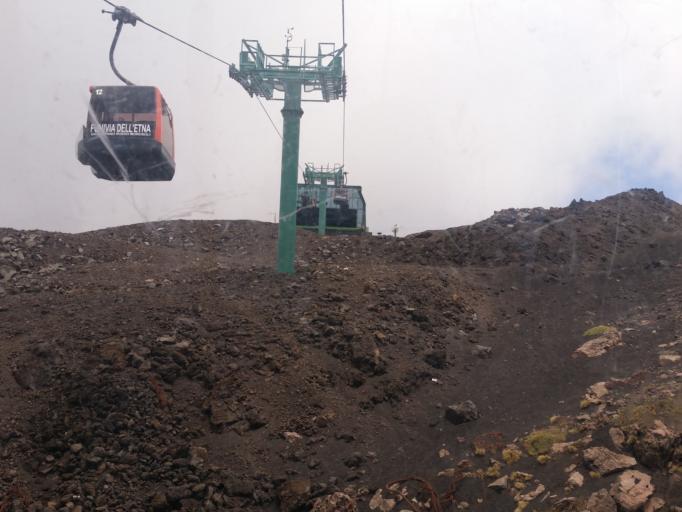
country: IT
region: Sicily
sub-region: Catania
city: Ragalna
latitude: 37.7171
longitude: 14.9999
